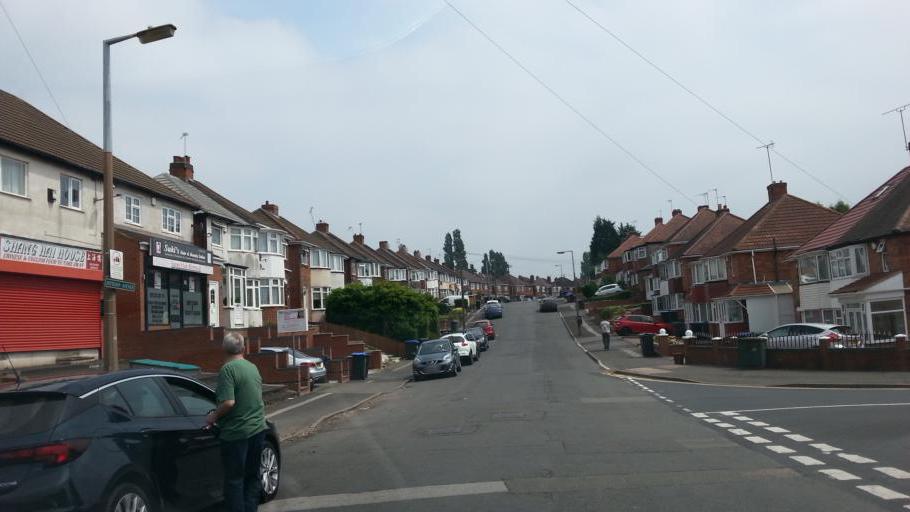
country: GB
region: England
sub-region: City and Borough of Birmingham
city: Hockley
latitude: 52.5432
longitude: -1.9382
